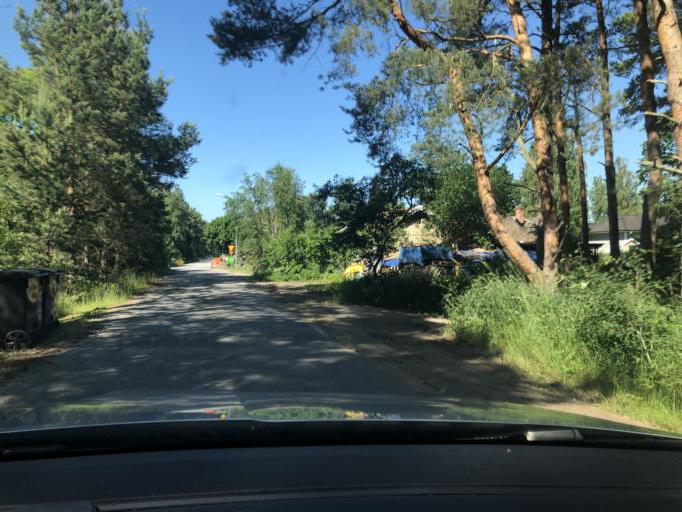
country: SE
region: Blekinge
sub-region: Karlshamns Kommun
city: Morrum
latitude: 56.1723
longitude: 14.7323
